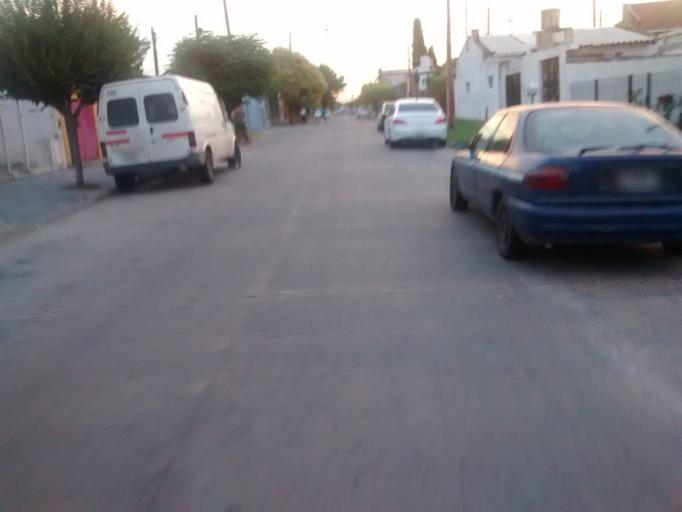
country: AR
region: Buenos Aires
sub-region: Partido de La Plata
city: La Plata
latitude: -34.9411
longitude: -57.9318
